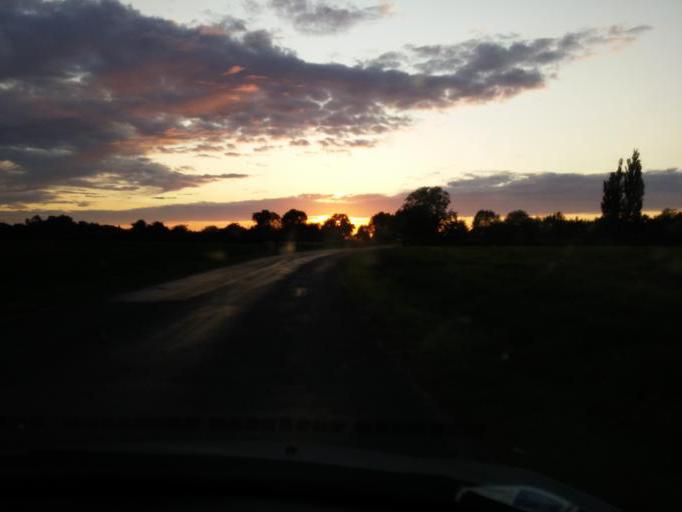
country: DK
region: South Denmark
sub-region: Kerteminde Kommune
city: Kerteminde
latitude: 55.4324
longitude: 10.6133
